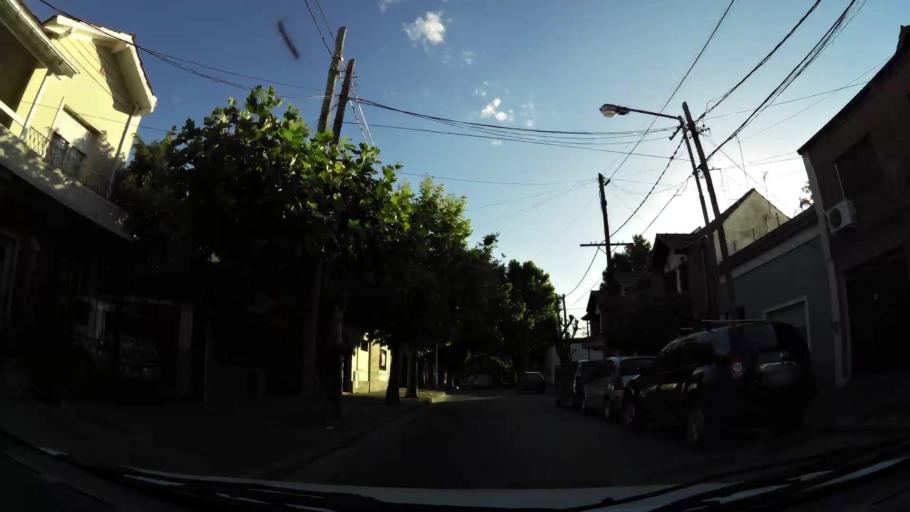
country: AR
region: Buenos Aires
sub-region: Partido de General San Martin
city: General San Martin
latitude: -34.5678
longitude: -58.5466
